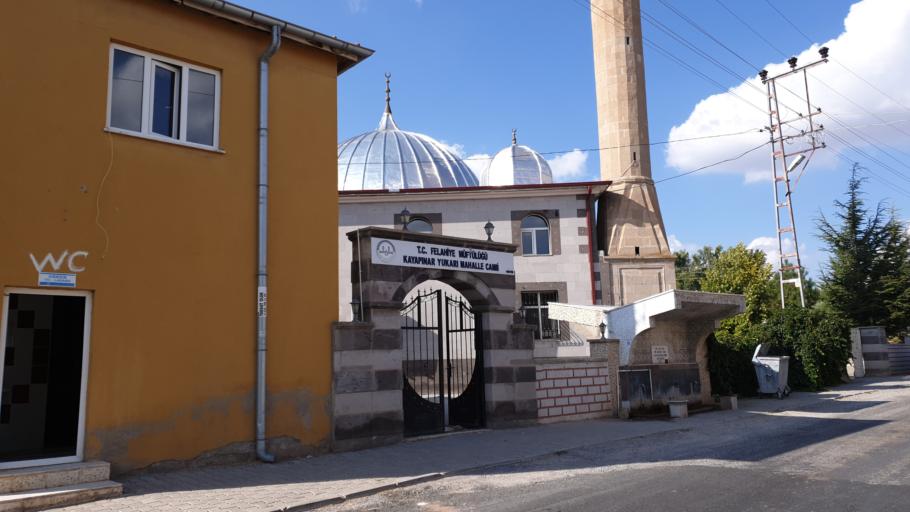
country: TR
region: Kayseri
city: Felahiye
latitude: 39.1158
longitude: 35.6138
